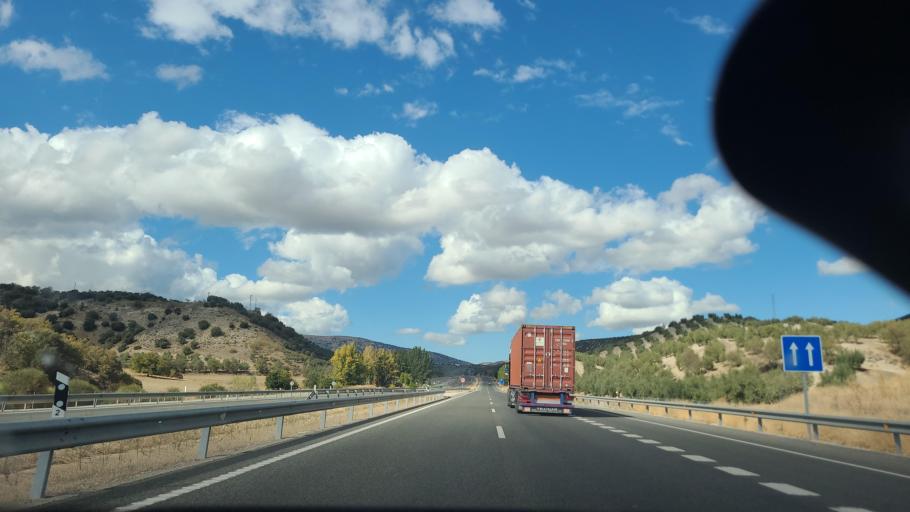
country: ES
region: Andalusia
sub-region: Provincia de Granada
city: Campotejar
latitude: 37.4993
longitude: -3.6271
